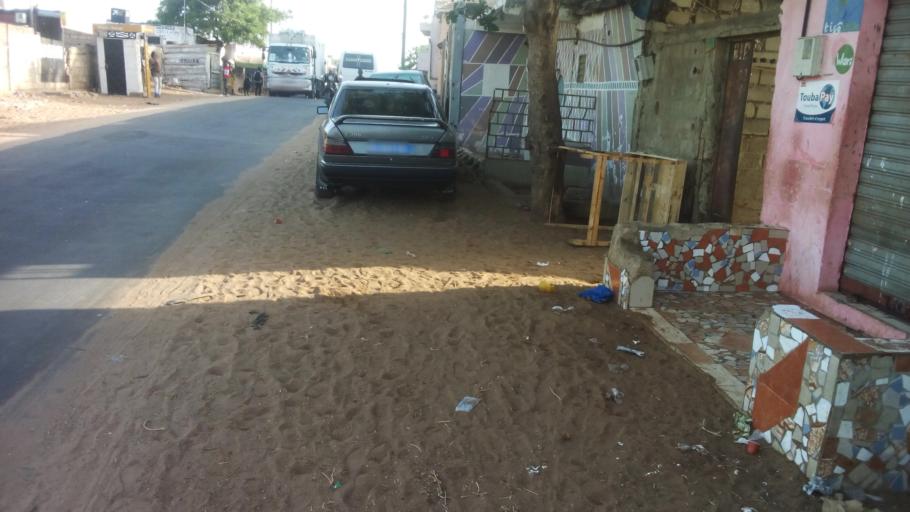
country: SN
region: Dakar
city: Pikine
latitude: 14.7966
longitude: -17.3368
